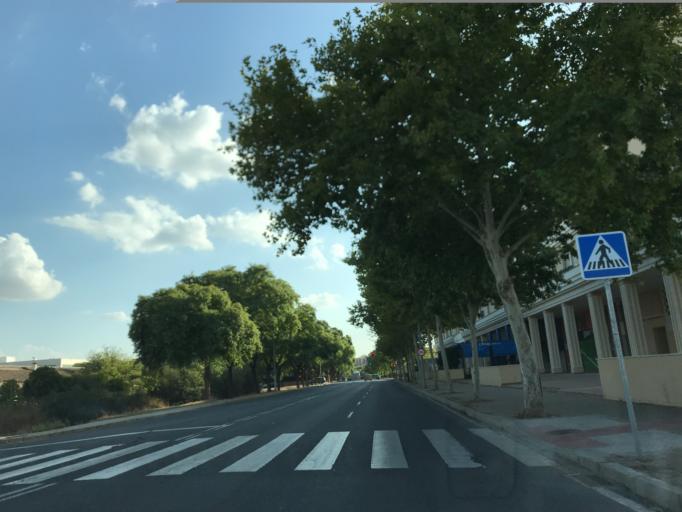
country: ES
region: Andalusia
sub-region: Provincia de Sevilla
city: Sevilla
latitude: 37.4101
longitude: -5.9333
